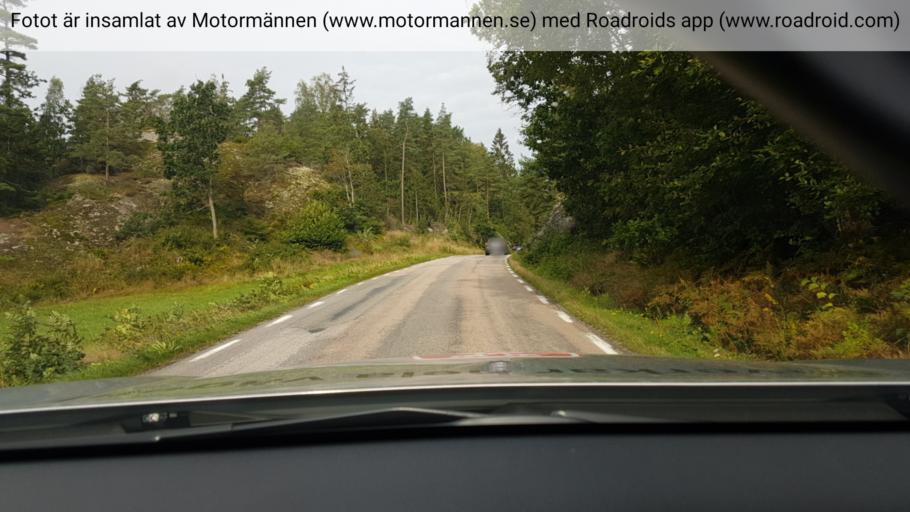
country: SE
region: Vaestra Goetaland
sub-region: Lysekils Kommun
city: Lysekil
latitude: 58.2565
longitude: 11.5470
